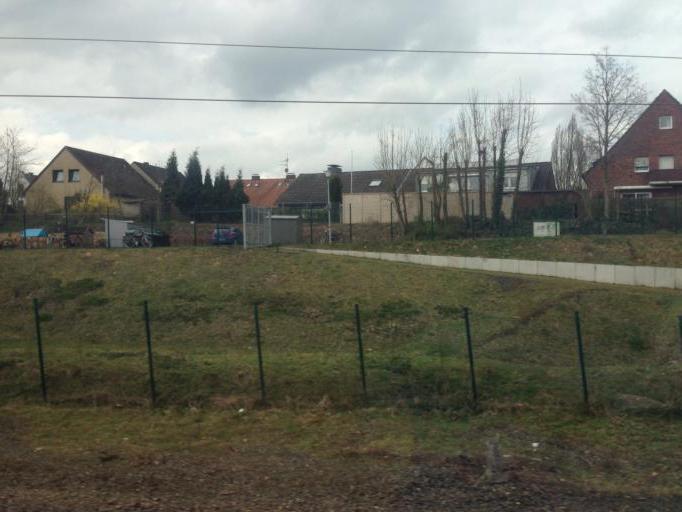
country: DE
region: North Rhine-Westphalia
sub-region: Regierungsbezirk Munster
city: Muenster
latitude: 51.9326
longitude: 7.6251
